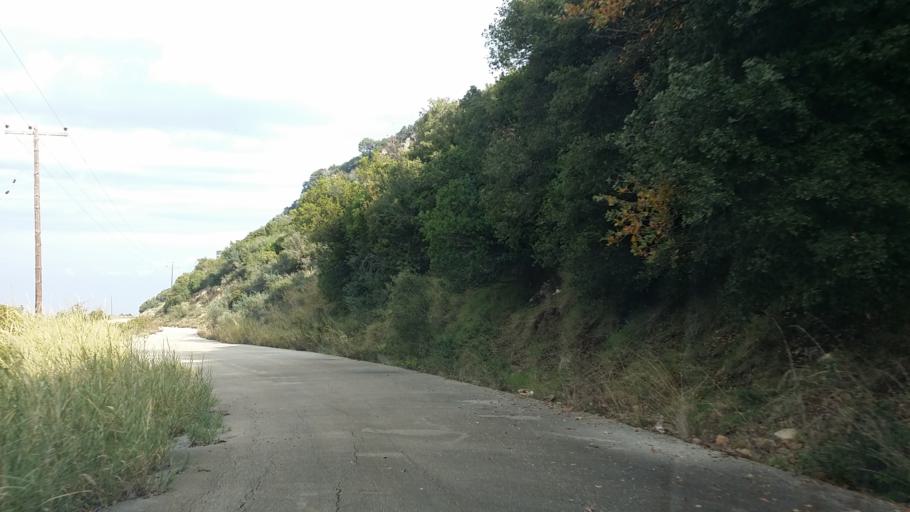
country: GR
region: West Greece
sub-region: Nomos Aitolias kai Akarnanias
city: Katouna
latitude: 38.8538
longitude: 21.0555
